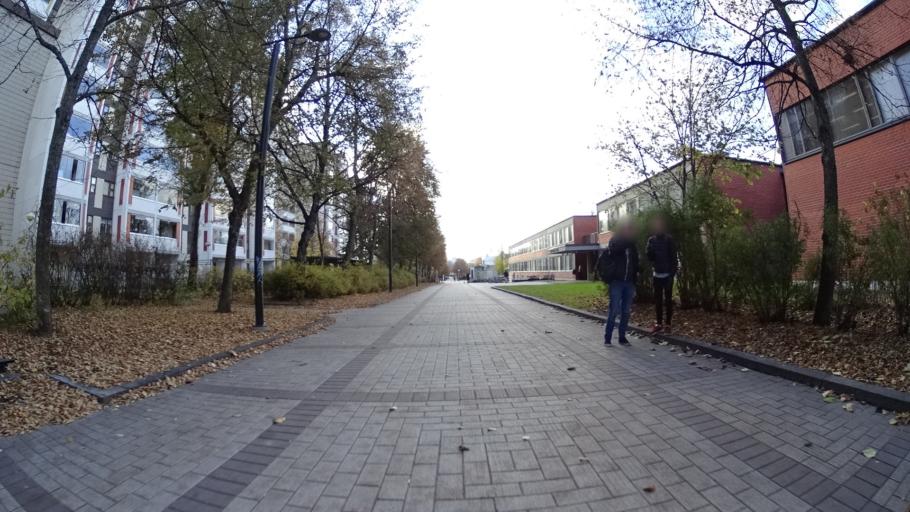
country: FI
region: Uusimaa
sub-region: Helsinki
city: Teekkarikylae
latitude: 60.2669
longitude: 24.8519
